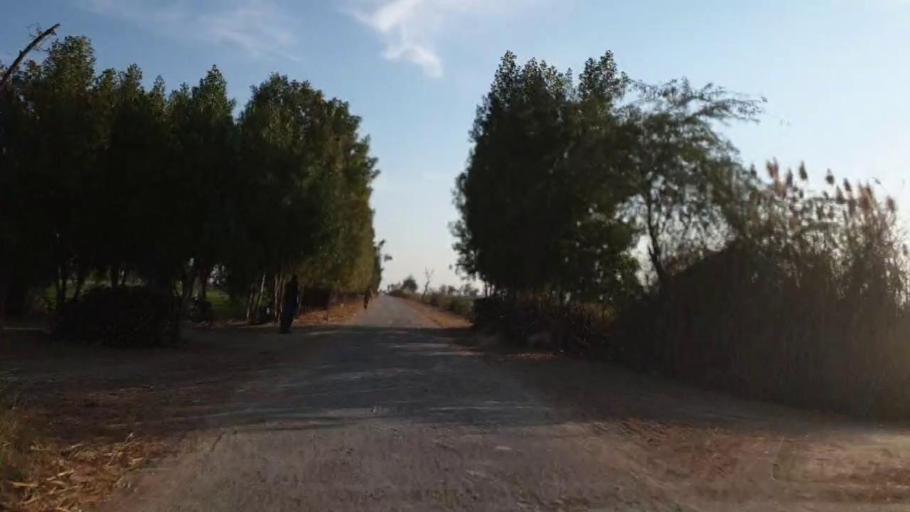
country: PK
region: Sindh
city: Khadro
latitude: 26.1852
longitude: 68.7499
